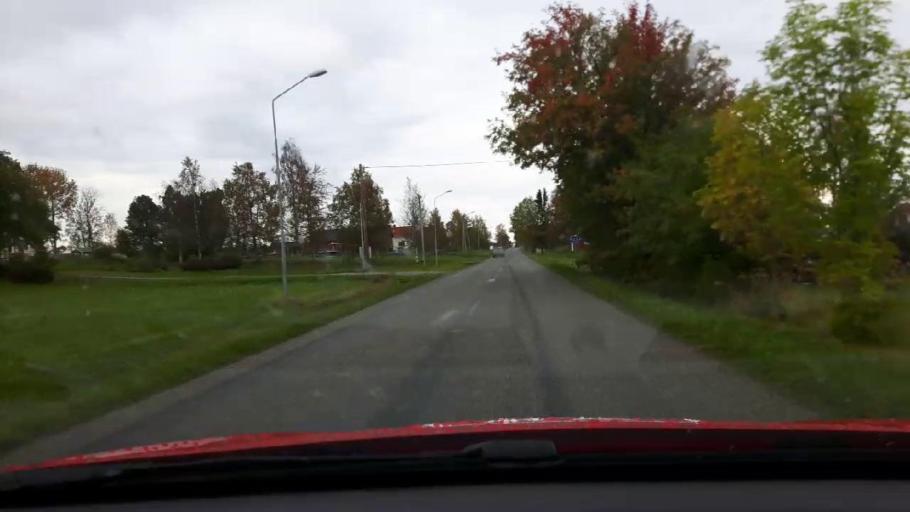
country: SE
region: Jaemtland
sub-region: Bergs Kommun
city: Hoverberg
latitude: 62.9635
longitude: 14.4896
